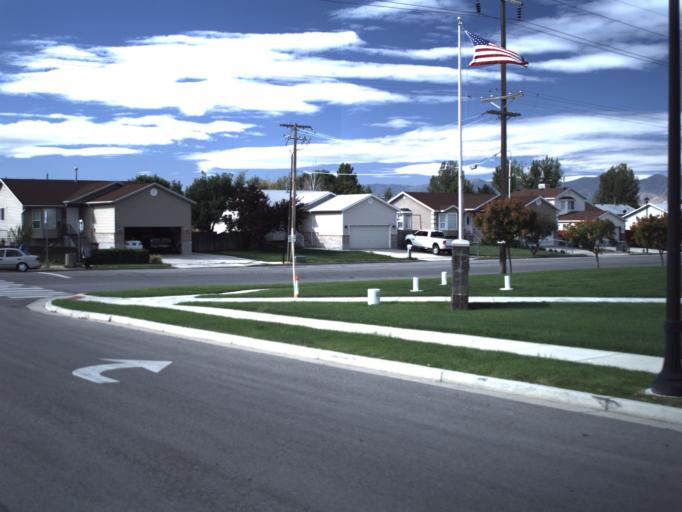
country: US
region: Utah
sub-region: Davis County
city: North Salt Lake
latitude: 40.8061
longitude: -111.9392
